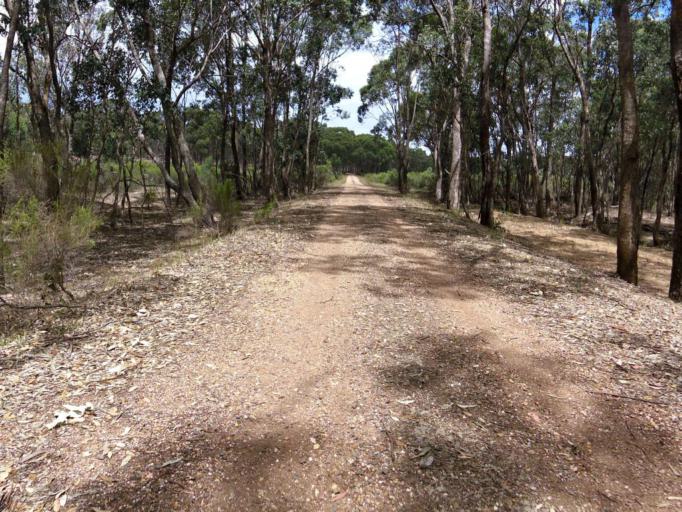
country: AU
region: Victoria
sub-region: Greater Bendigo
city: Kennington
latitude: -36.8869
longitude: 144.6579
